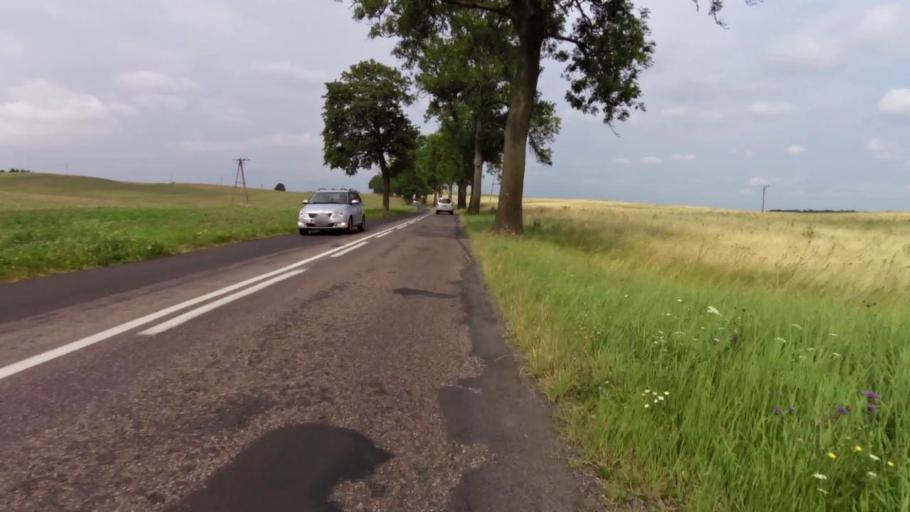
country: PL
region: West Pomeranian Voivodeship
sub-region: Powiat drawski
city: Drawsko Pomorskie
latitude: 53.5562
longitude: 15.8265
